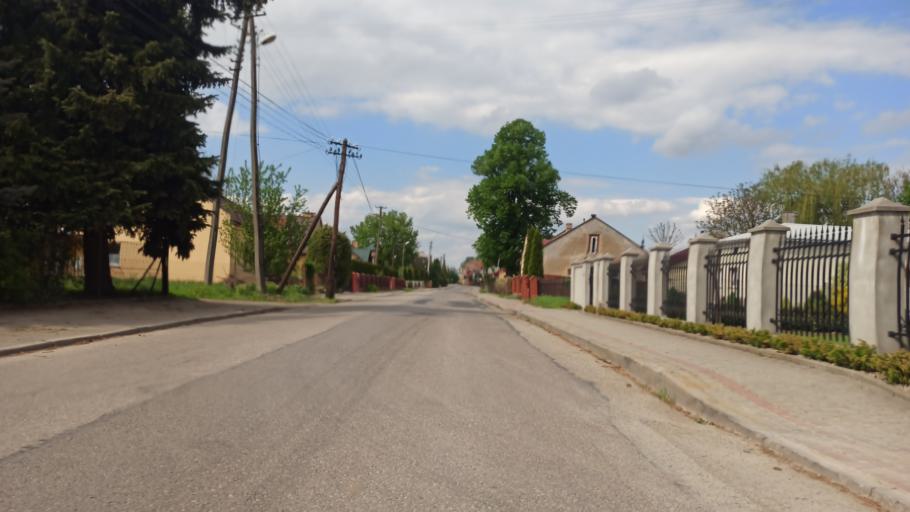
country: PL
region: Subcarpathian Voivodeship
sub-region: Powiat jaroslawski
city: Radymno
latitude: 49.9487
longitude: 22.8149
